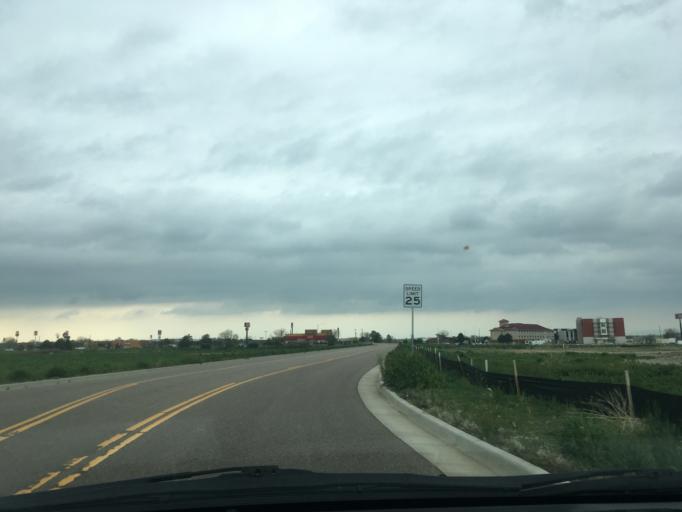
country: US
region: Colorado
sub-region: Weld County
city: Firestone
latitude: 40.1632
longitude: -104.9719
